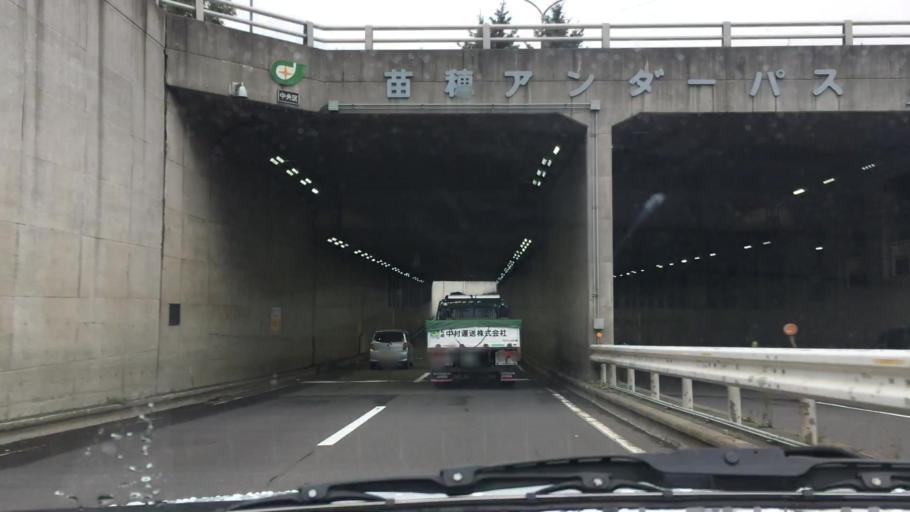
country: JP
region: Hokkaido
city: Sapporo
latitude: 43.0698
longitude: 141.3810
